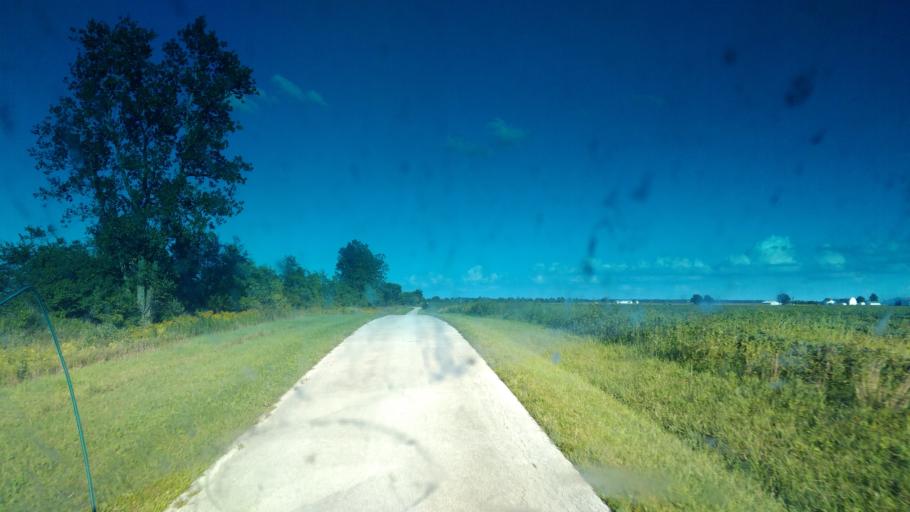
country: US
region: Ohio
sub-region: Wyandot County
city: Carey
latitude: 40.9413
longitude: -83.4344
